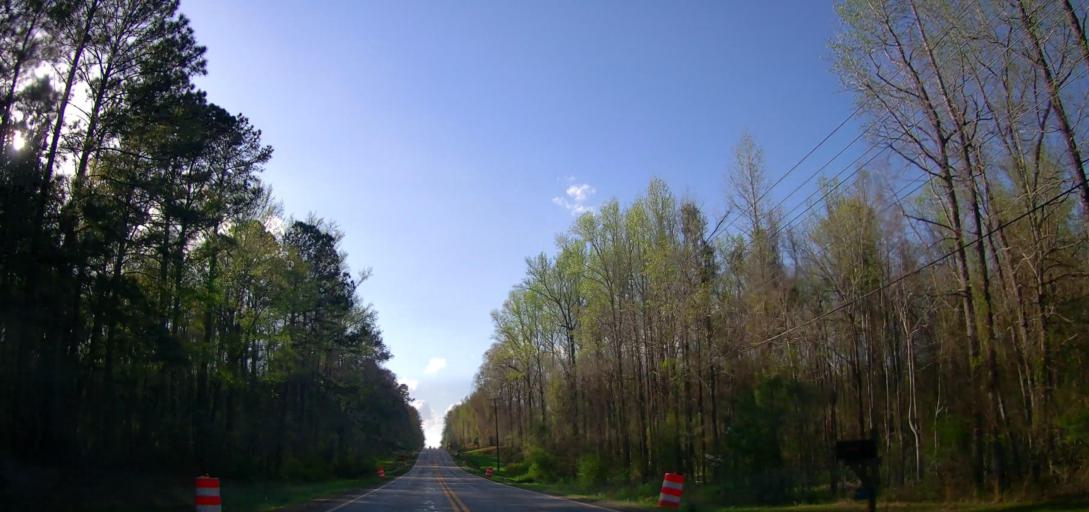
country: US
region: Georgia
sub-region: Putnam County
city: Eatonton
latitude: 33.1667
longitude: -83.3817
